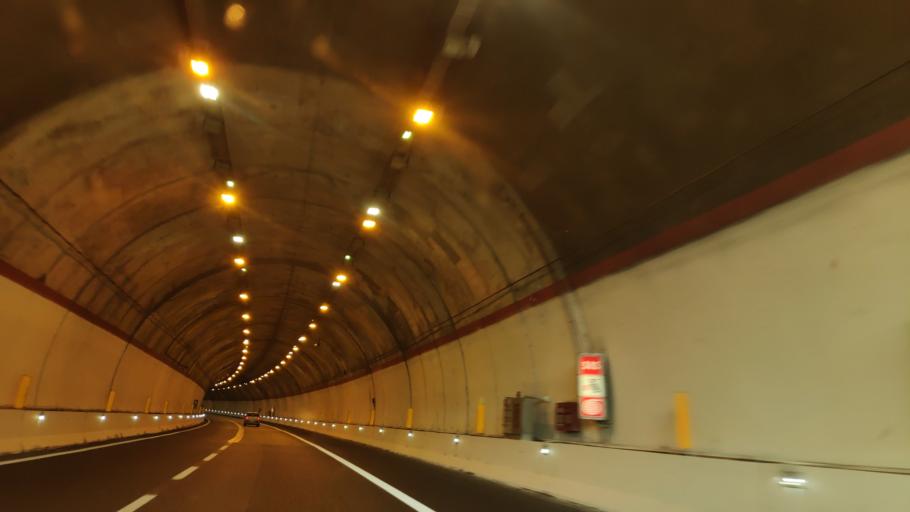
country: IT
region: Calabria
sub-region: Provincia di Reggio Calabria
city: Ceramida-Pellegrina
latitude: 38.2944
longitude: 15.8406
